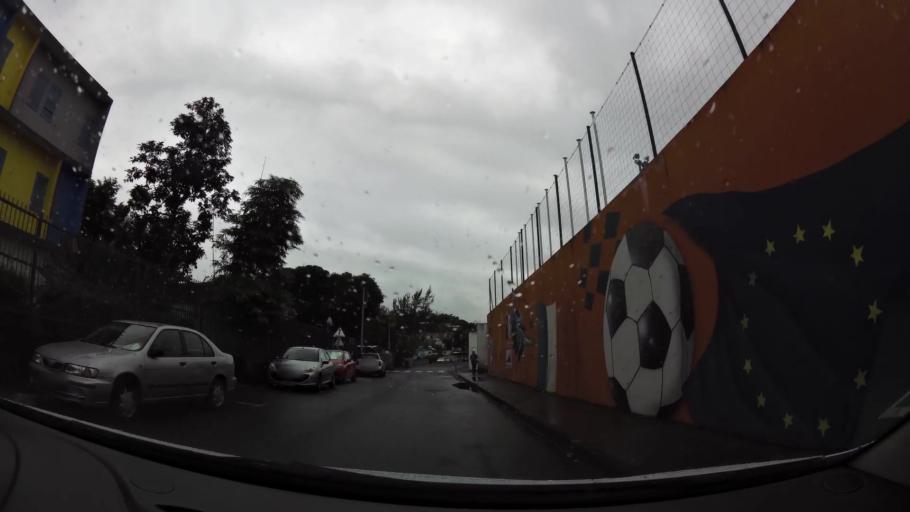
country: RE
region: Reunion
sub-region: Reunion
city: Saint-Andre
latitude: -20.9574
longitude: 55.6484
